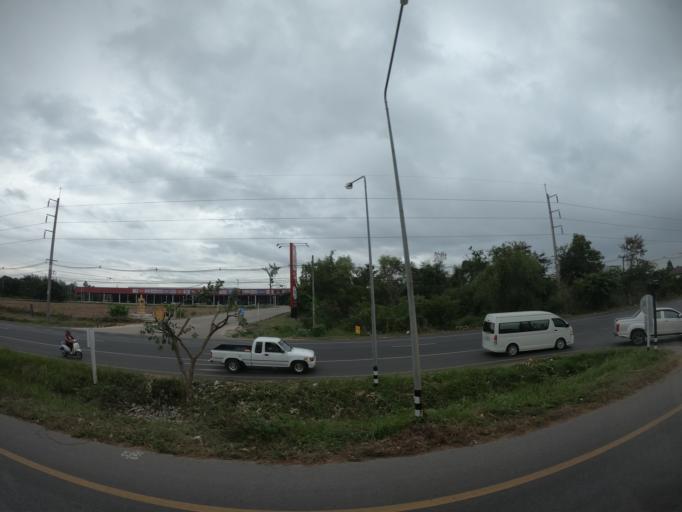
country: TH
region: Roi Et
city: Roi Et
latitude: 16.0548
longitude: 103.6200
